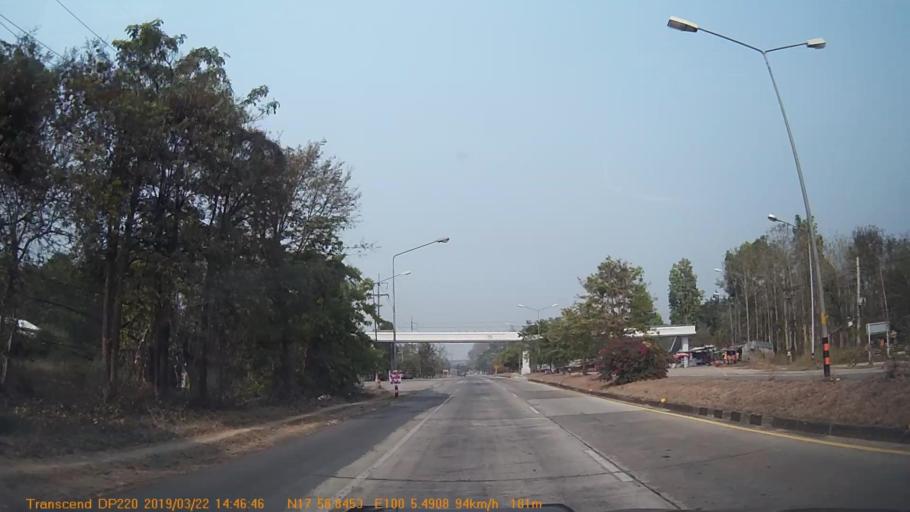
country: TH
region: Phrae
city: Den Chai
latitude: 17.9811
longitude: 100.0917
